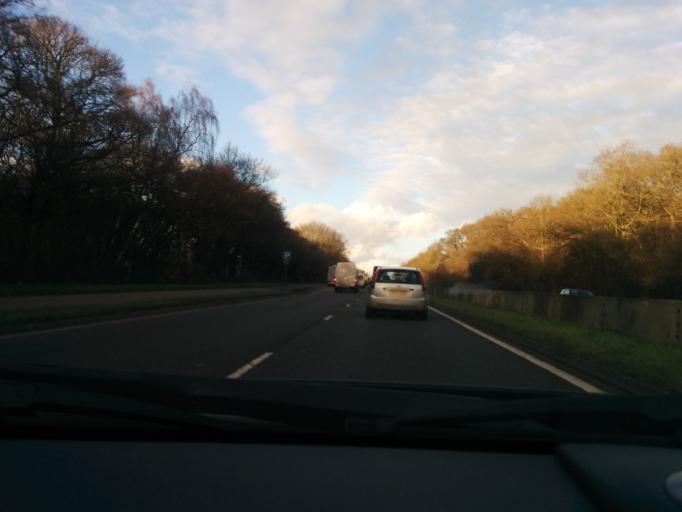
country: GB
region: England
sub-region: Oxfordshire
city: Cowley
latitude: 51.7477
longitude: -1.1954
